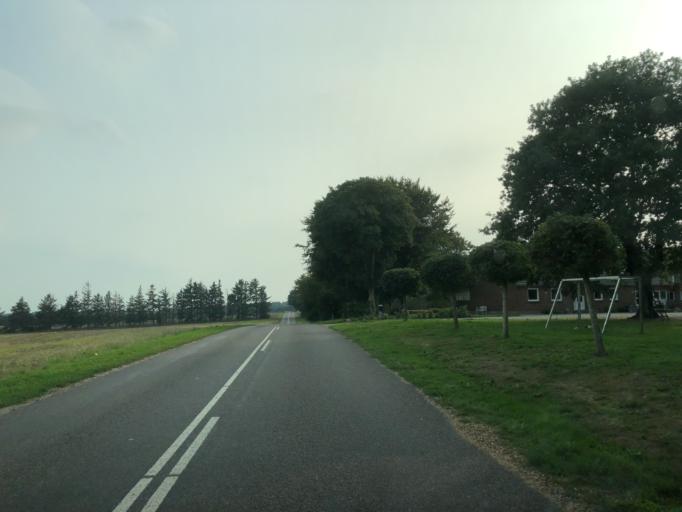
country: DK
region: Central Jutland
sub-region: Ringkobing-Skjern Kommune
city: Videbaek
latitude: 56.0738
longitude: 8.7011
